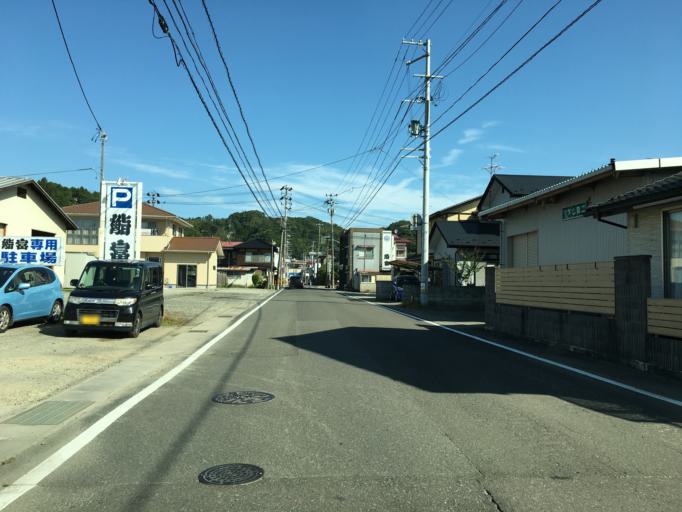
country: JP
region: Fukushima
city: Nihommatsu
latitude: 37.5887
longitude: 140.4271
